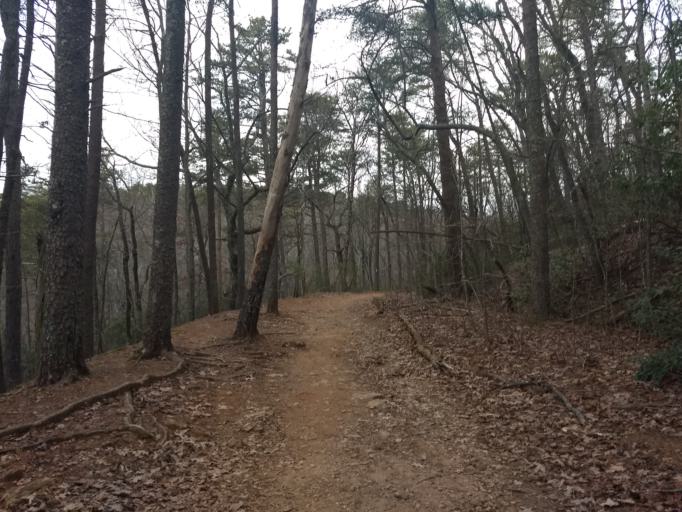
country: US
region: South Carolina
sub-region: Greenville County
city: Travelers Rest
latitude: 34.9419
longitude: -82.3938
